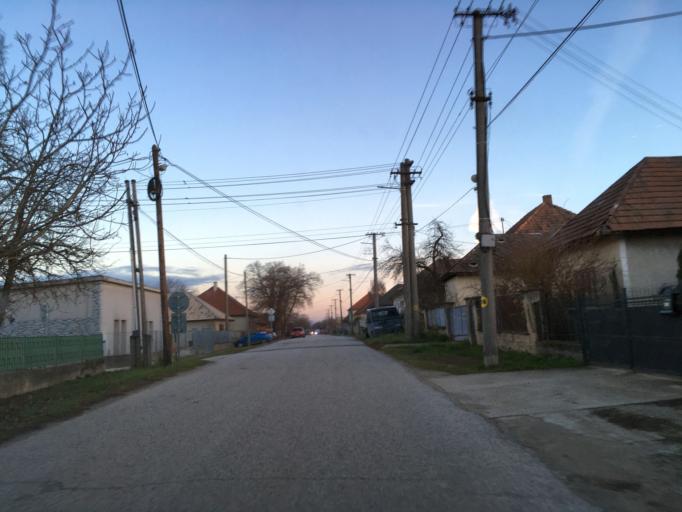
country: SK
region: Nitriansky
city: Svodin
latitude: 47.8678
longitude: 18.4670
